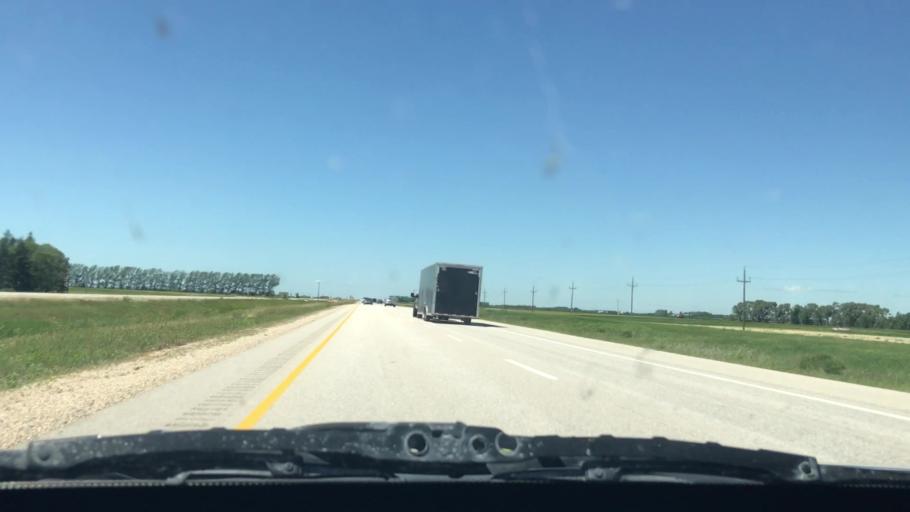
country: CA
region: Manitoba
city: Steinbach
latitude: 49.7313
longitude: -96.7214
